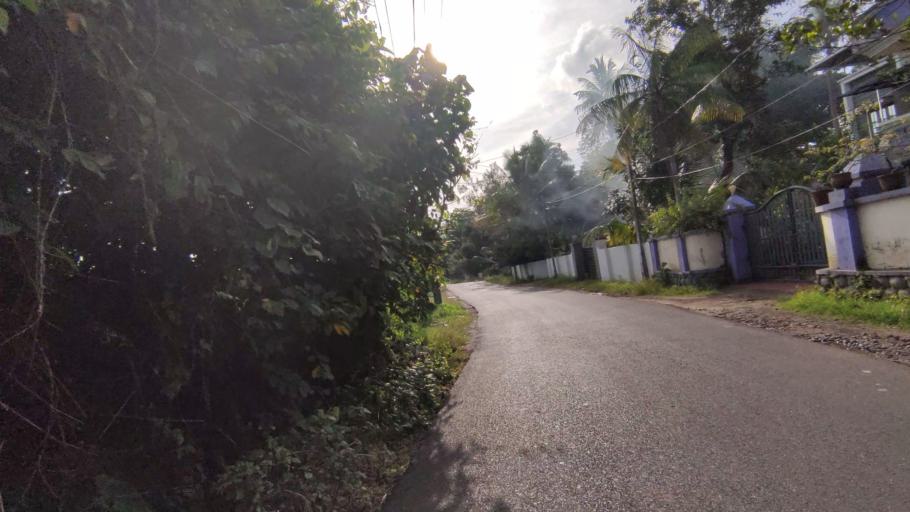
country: IN
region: Kerala
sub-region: Kottayam
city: Kottayam
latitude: 9.5784
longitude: 76.5003
